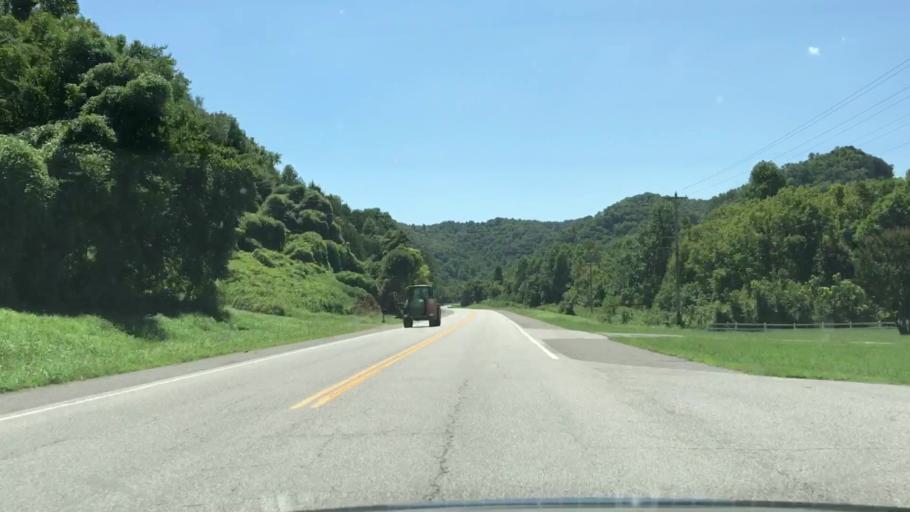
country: US
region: Tennessee
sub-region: Clay County
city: Celina
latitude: 36.4896
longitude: -85.5620
